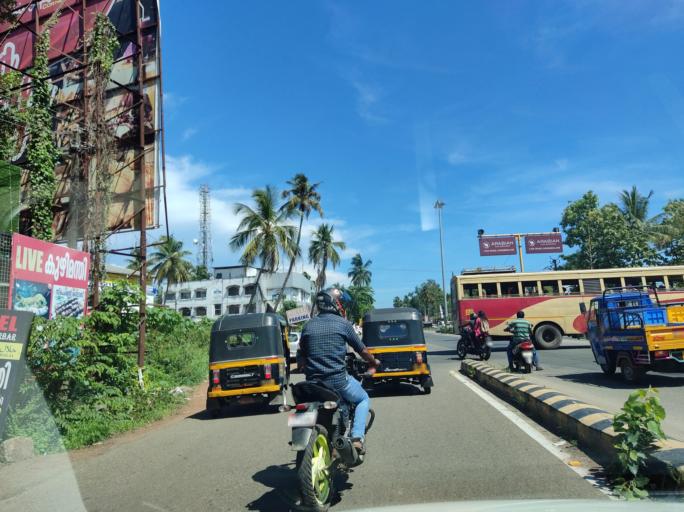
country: IN
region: Kerala
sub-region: Alappuzha
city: Kayankulam
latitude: 9.1710
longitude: 76.4983
